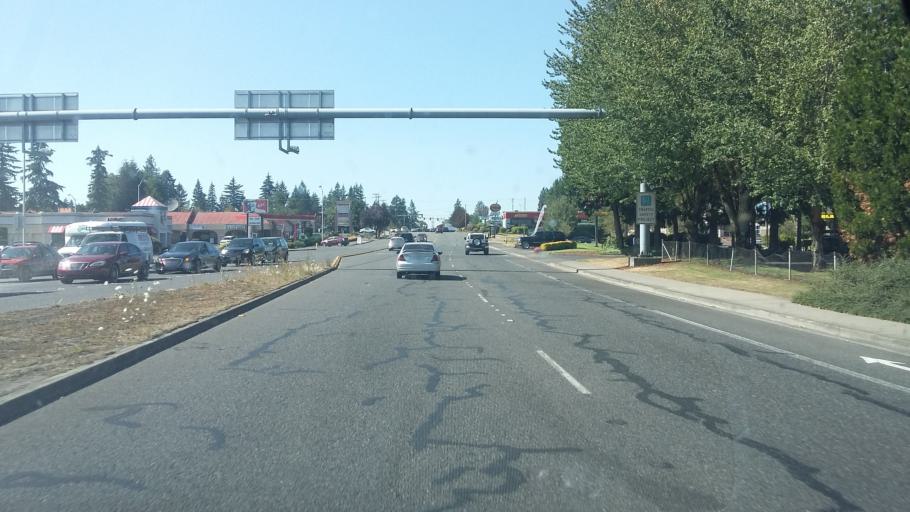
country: US
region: Washington
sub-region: Clark County
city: Orchards
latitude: 45.6620
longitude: -122.5591
